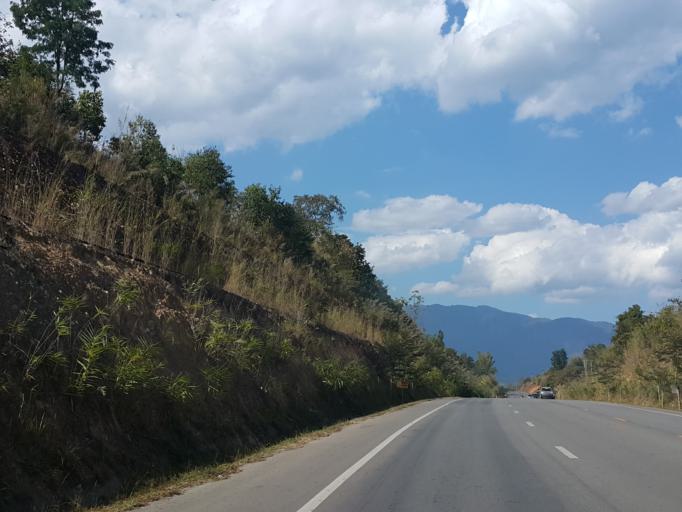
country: TH
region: Chiang Mai
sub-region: Amphoe Chiang Dao
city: Chiang Dao
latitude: 19.3568
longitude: 98.9548
